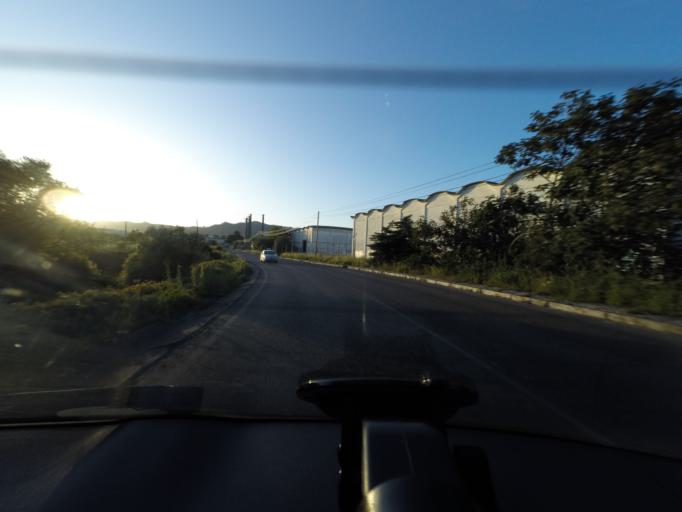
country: PT
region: Lisbon
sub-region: Sintra
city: Rio de Mouro
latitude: 38.7594
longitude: -9.3624
